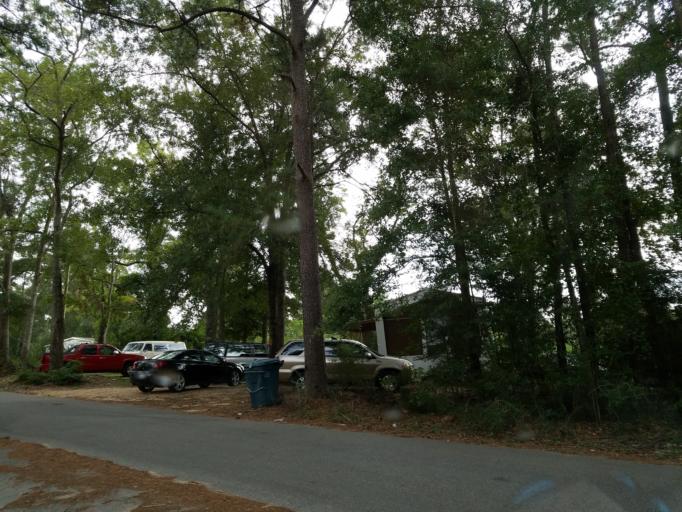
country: US
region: Mississippi
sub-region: Wayne County
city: Belmont
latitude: 31.4385
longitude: -88.4782
